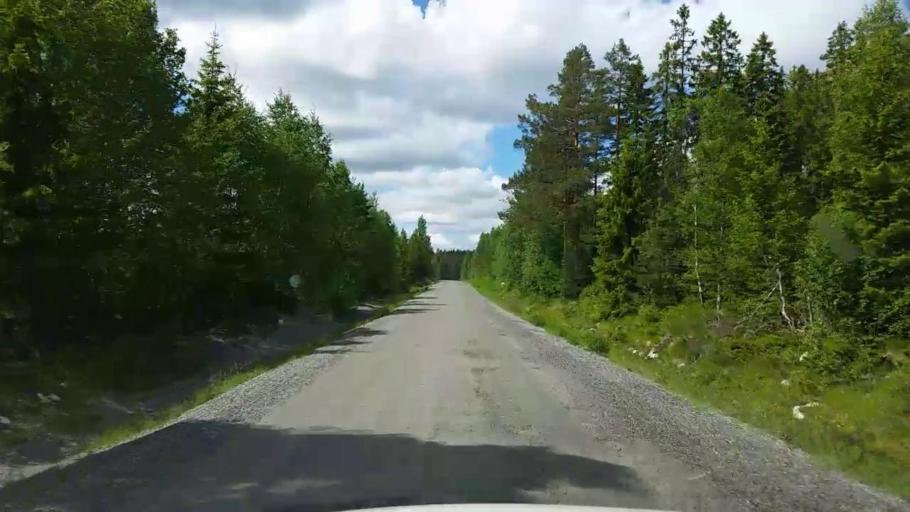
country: SE
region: Gaevleborg
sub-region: Bollnas Kommun
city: Vittsjo
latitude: 61.0900
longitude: 16.1829
